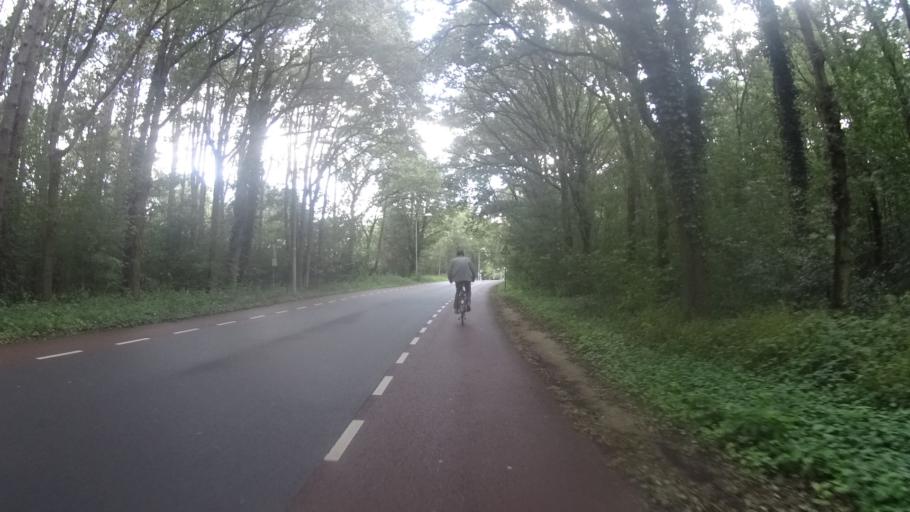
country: NL
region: North Holland
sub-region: Gemeente Bloemendaal
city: Bloemendaal
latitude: 52.4260
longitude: 4.6323
